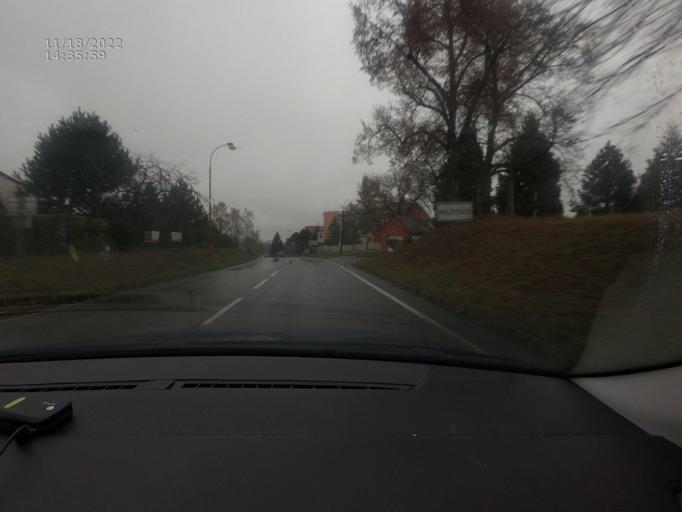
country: CZ
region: Jihocesky
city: Milevsko
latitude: 49.4526
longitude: 14.3507
